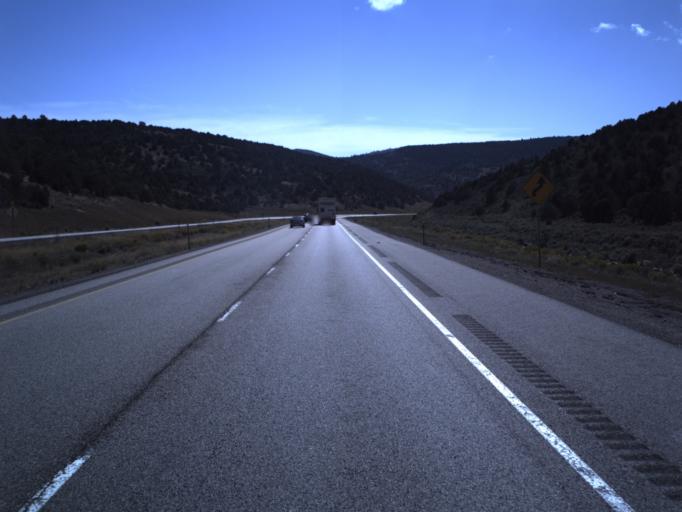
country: US
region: Utah
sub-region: Wayne County
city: Loa
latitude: 38.7760
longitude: -111.4779
